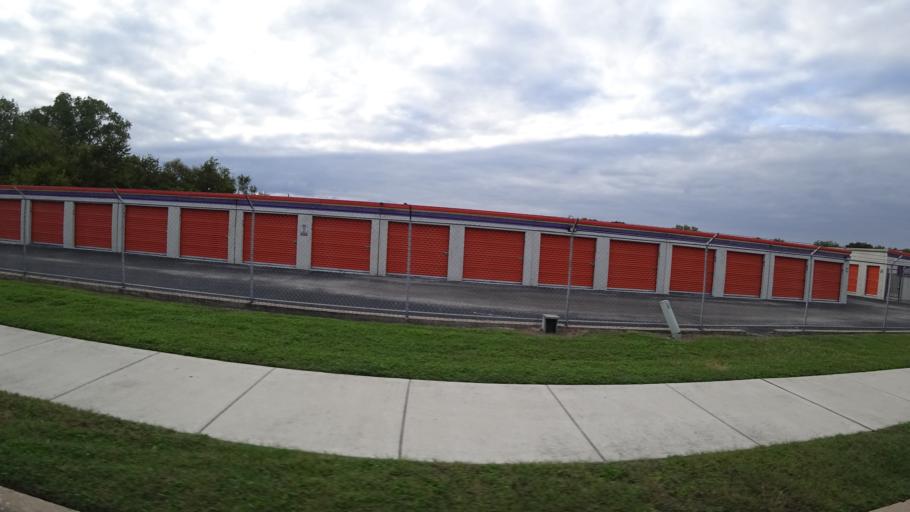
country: US
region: Texas
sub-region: Travis County
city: Onion Creek
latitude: 30.1914
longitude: -97.7907
